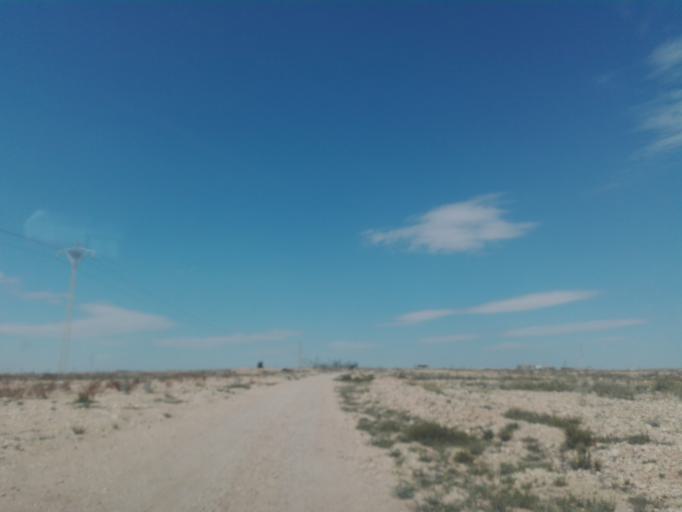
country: TN
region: Safaqis
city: Sfax
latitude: 34.6875
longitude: 10.5432
